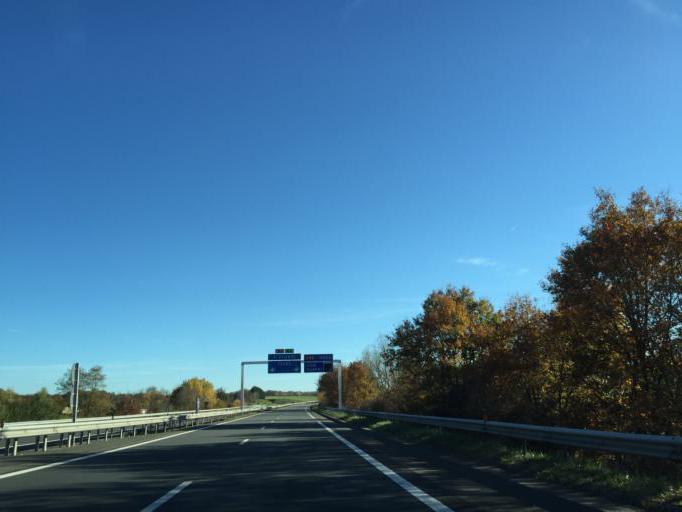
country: FR
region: Rhone-Alpes
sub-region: Departement de la Loire
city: Balbigny
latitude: 45.8263
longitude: 4.1063
